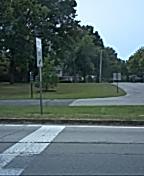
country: US
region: Kentucky
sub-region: Jefferson County
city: Douglass Hills
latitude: 38.2456
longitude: -85.5669
